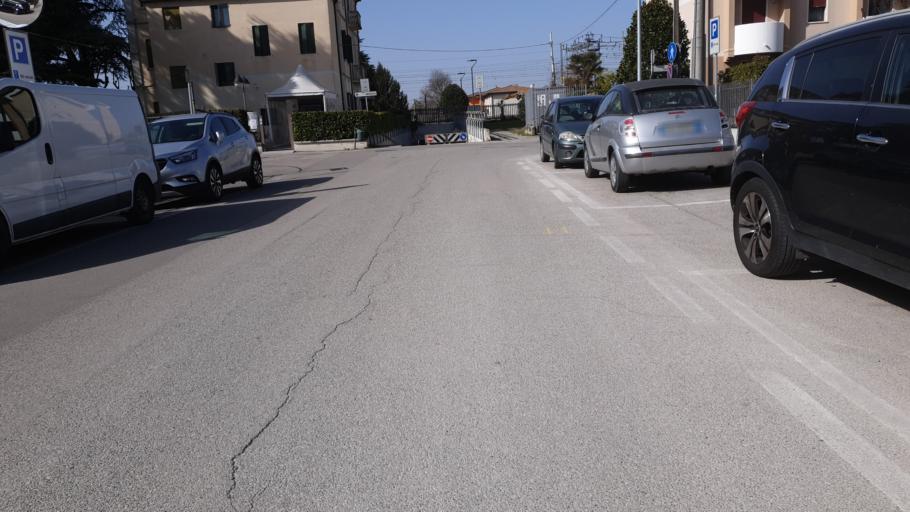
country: IT
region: Veneto
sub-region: Provincia di Padova
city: Camposampiero
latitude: 45.5661
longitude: 11.9282
